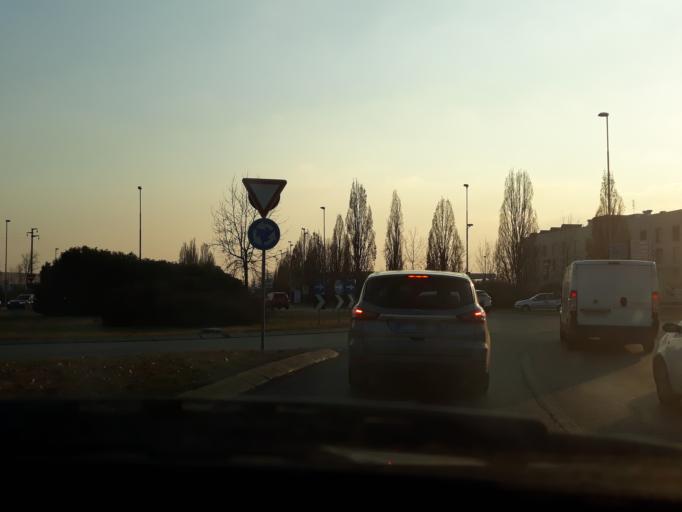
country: IT
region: Lombardy
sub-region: Provincia di Monza e Brianza
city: Villasanta
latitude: 45.5815
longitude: 9.3097
